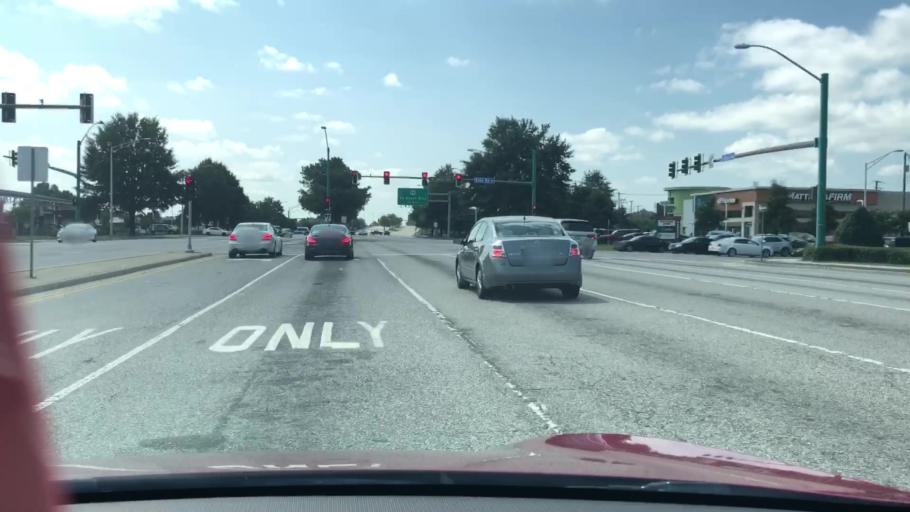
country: US
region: Virginia
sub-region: City of Norfolk
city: Norfolk
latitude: 36.8621
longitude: -76.2103
